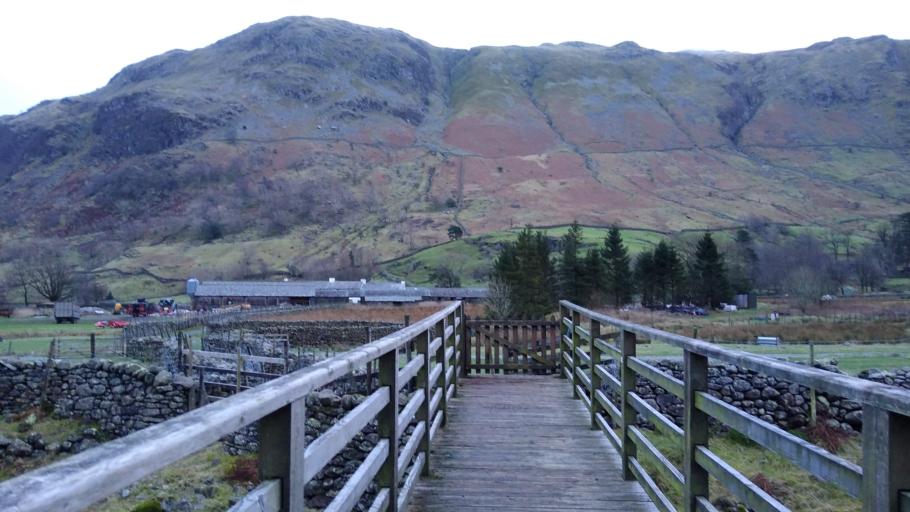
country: GB
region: England
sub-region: Cumbria
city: Keswick
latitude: 54.4994
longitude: -3.1850
